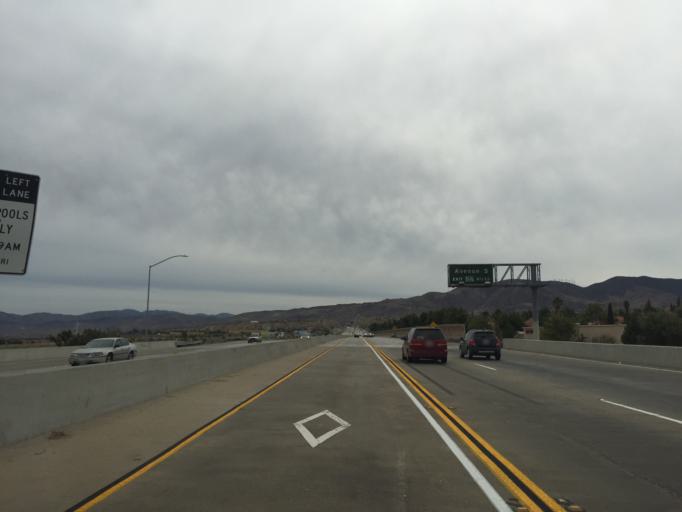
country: US
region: California
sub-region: Los Angeles County
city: Palmdale
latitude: 34.5819
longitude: -118.1338
